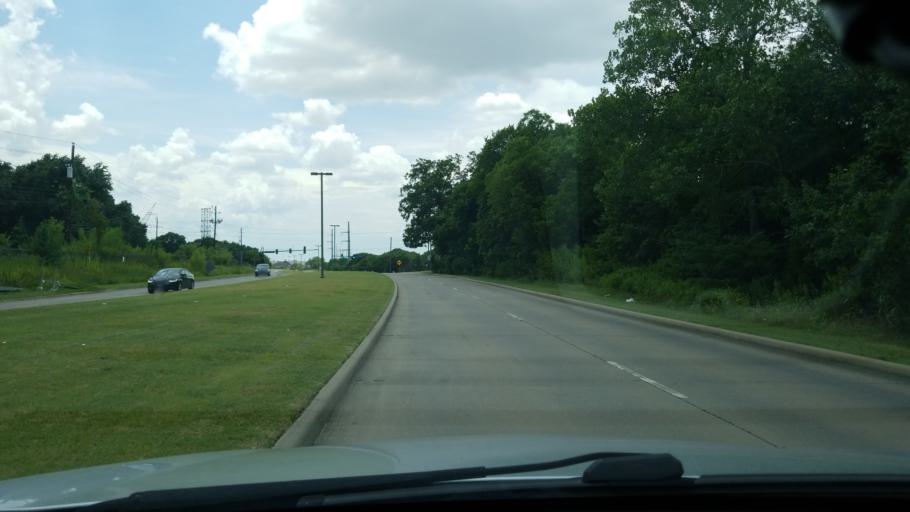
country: US
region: Texas
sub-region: Dallas County
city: Coppell
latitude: 32.9554
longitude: -96.9746
